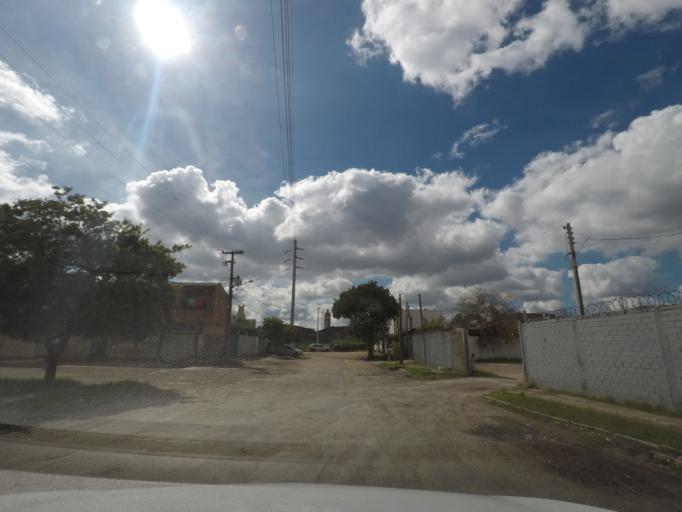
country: BR
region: Parana
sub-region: Sao Jose Dos Pinhais
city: Sao Jose dos Pinhais
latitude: -25.4933
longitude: -49.2289
